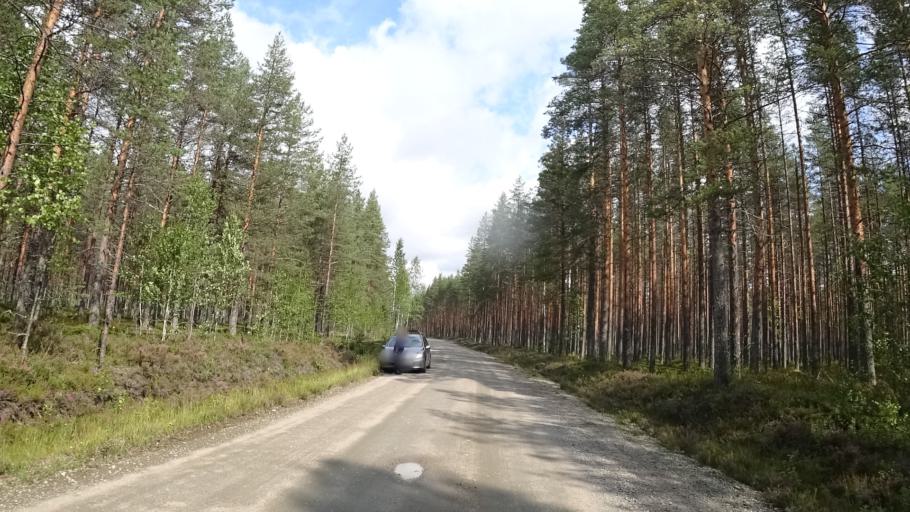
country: FI
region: North Karelia
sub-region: Joensuu
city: Ilomantsi
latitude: 62.9345
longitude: 31.4290
